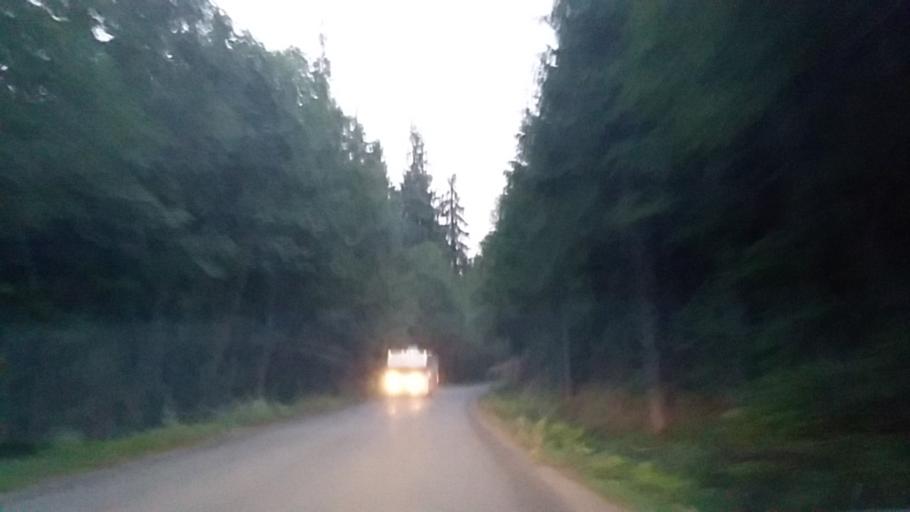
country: US
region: Washington
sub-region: Kittitas County
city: Cle Elum
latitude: 47.3540
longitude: -121.2528
